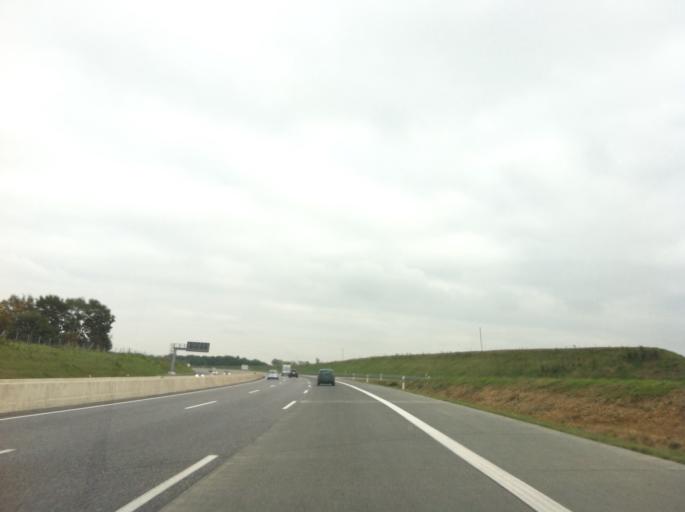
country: DE
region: North Rhine-Westphalia
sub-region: Regierungsbezirk Koln
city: Merzenich
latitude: 50.8470
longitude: 6.5169
